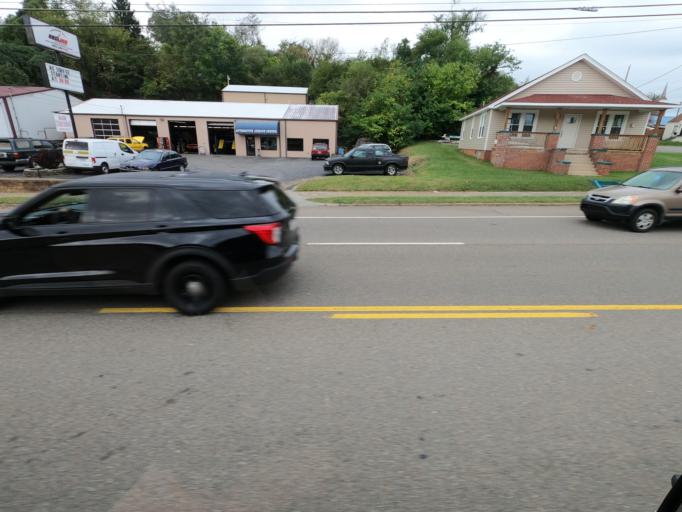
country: US
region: Tennessee
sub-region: Sullivan County
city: Kingsport
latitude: 36.5749
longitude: -82.5671
